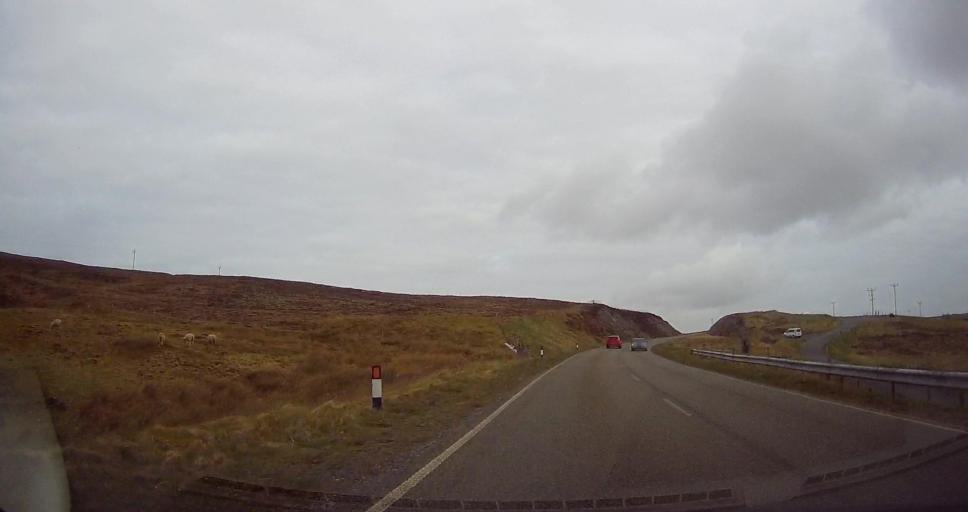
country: GB
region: Scotland
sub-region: Shetland Islands
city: Sandwick
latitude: 60.0729
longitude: -1.2311
